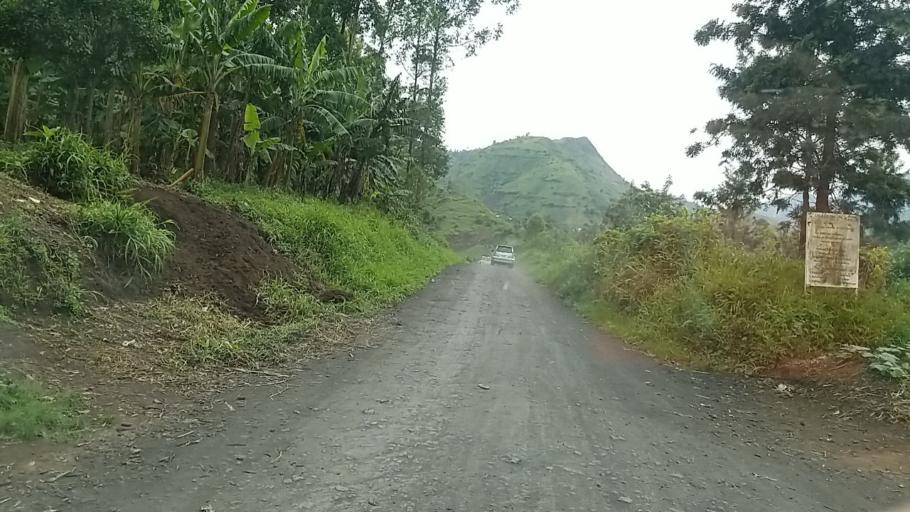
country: CD
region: Nord Kivu
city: Sake
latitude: -1.7322
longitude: 29.0074
